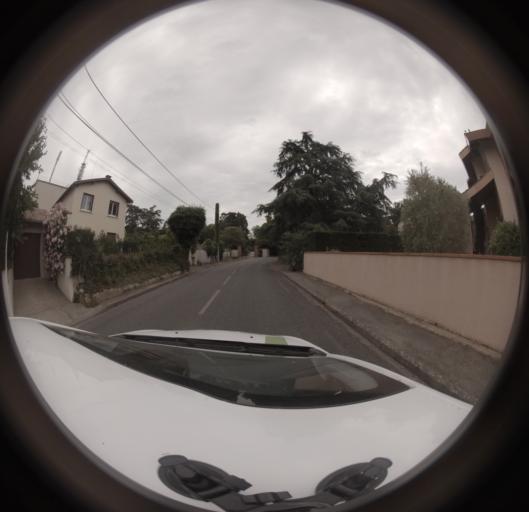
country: FR
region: Midi-Pyrenees
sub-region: Departement du Tarn-et-Garonne
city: Montauban
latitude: 44.0041
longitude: 1.3748
